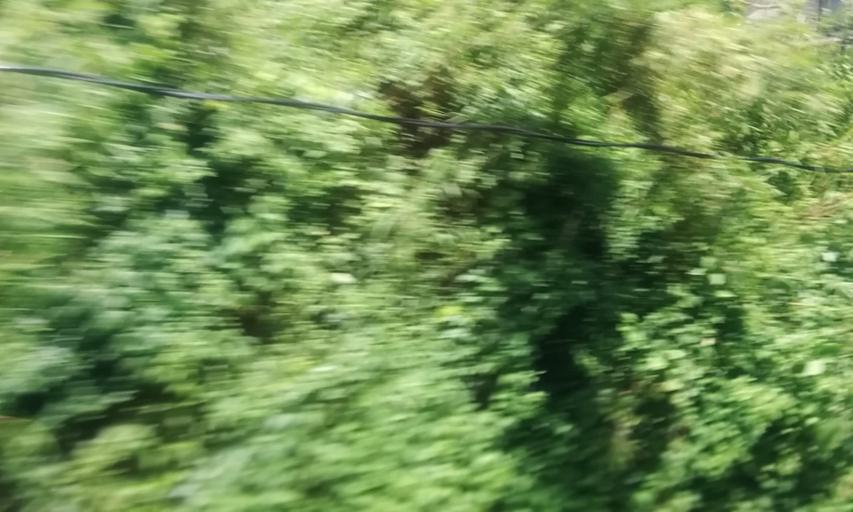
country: JP
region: Chiba
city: Oami
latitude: 35.5330
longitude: 140.2638
